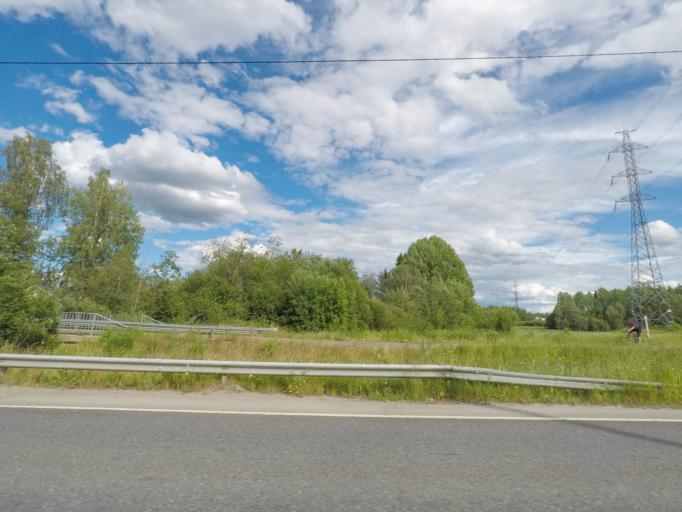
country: FI
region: Paijanne Tavastia
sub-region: Lahti
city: Lahti
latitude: 60.9597
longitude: 25.6213
